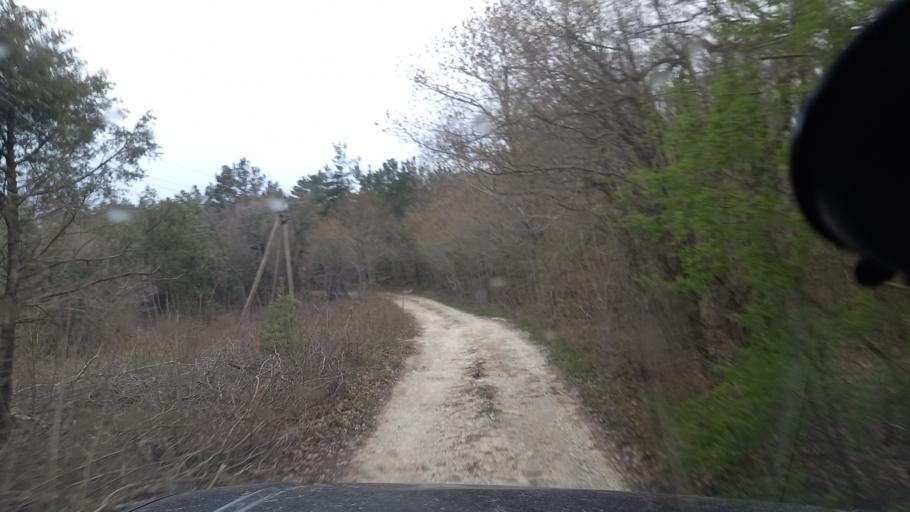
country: RU
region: Krasnodarskiy
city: Dzhubga
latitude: 44.3199
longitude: 38.6716
